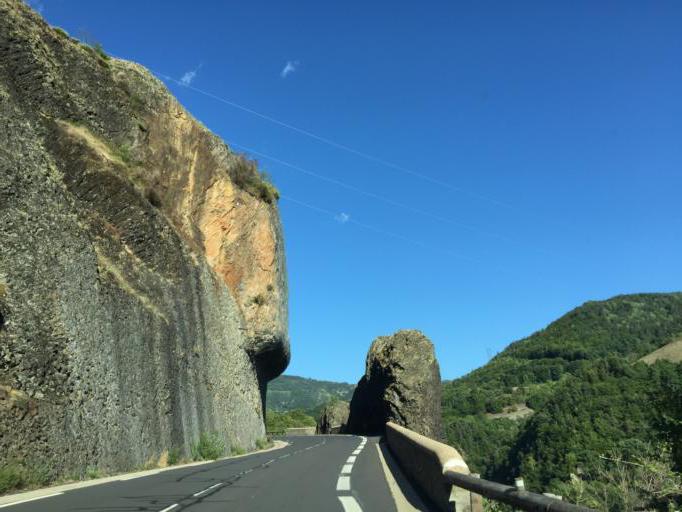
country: FR
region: Auvergne
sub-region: Departement de la Haute-Loire
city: Saugues
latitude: 44.9701
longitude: 3.6565
